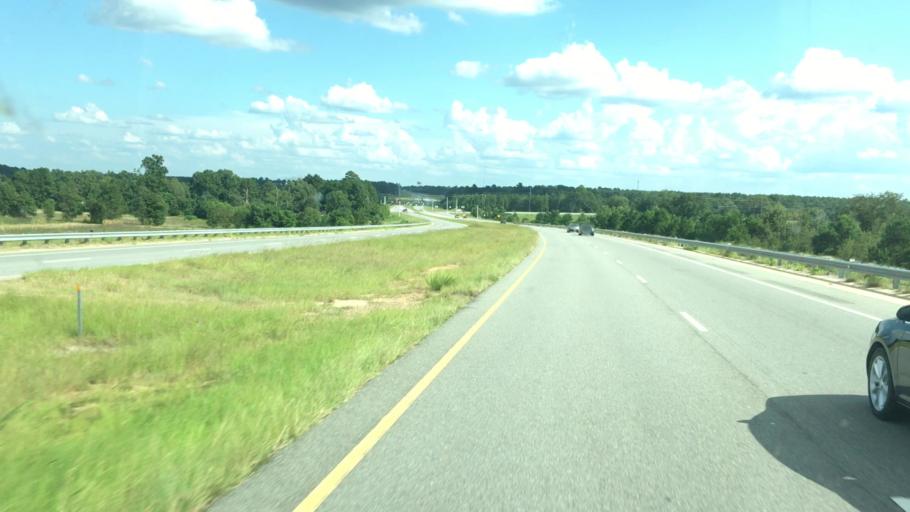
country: US
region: Georgia
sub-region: Laurens County
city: Dublin
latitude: 32.5204
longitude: -82.9612
